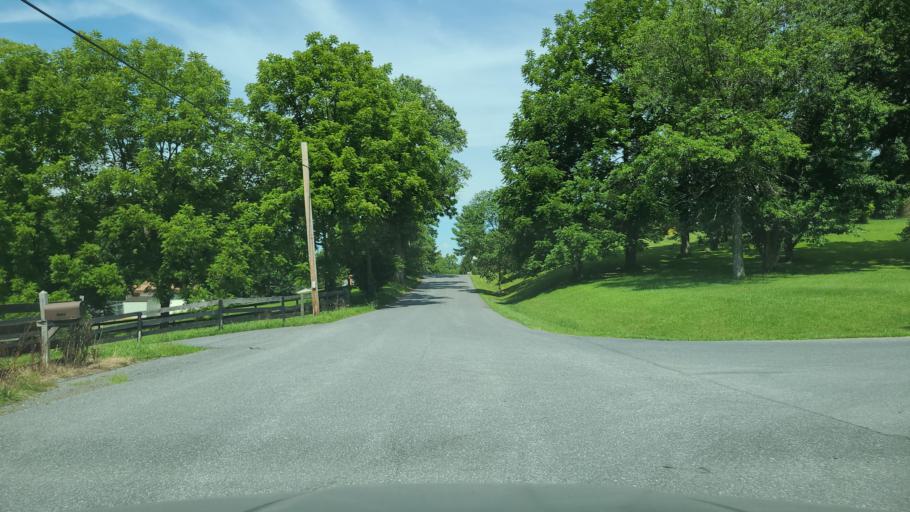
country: US
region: Maryland
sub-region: Frederick County
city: Green Valley
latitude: 39.3088
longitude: -77.2947
